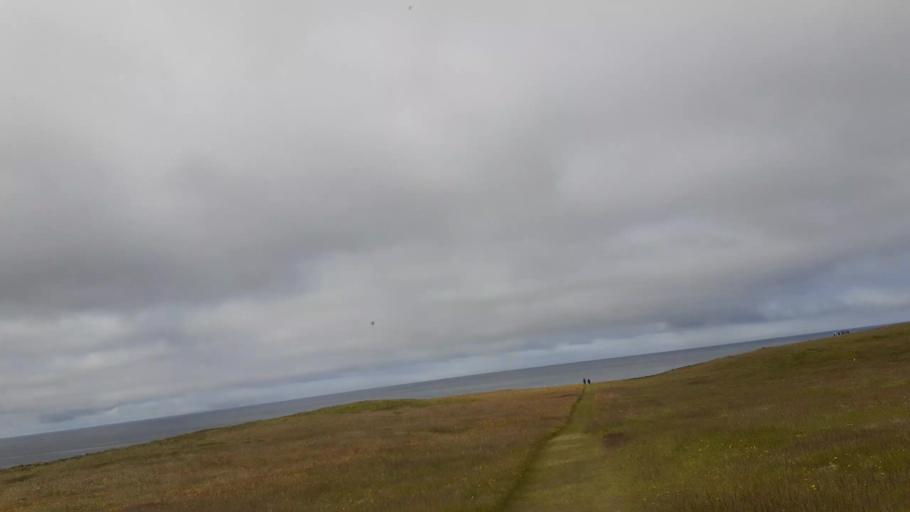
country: IS
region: Northeast
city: Dalvik
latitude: 66.5487
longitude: -18.0220
